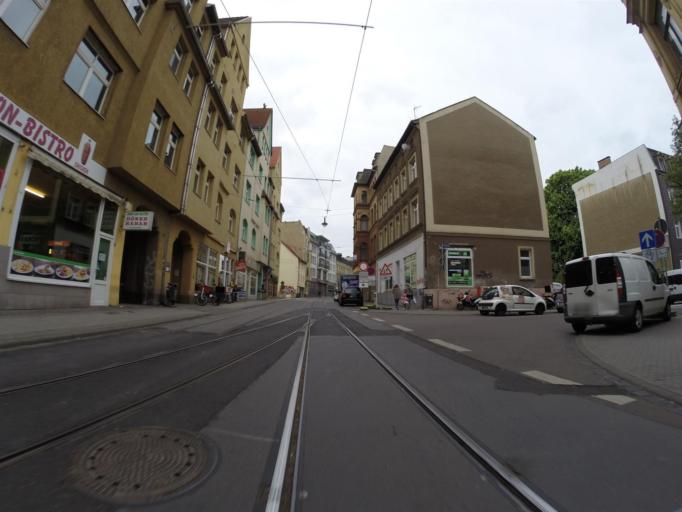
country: DE
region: Saxony-Anhalt
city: Halle (Saale)
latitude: 51.4755
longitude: 11.9699
